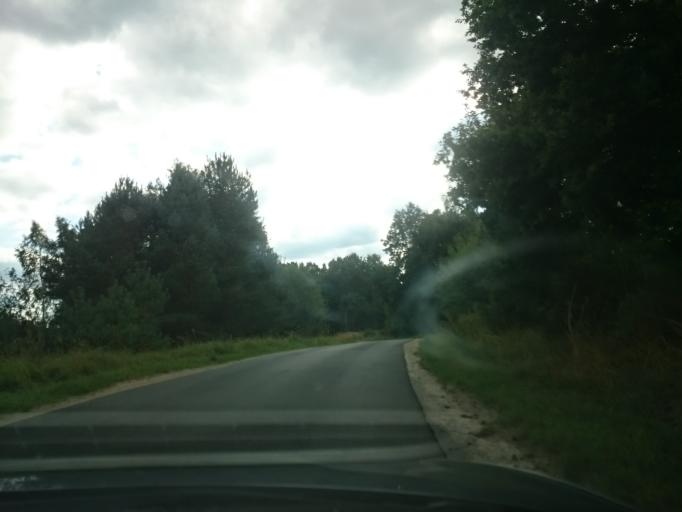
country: DE
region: Mecklenburg-Vorpommern
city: Carpin
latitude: 53.3636
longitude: 13.2496
